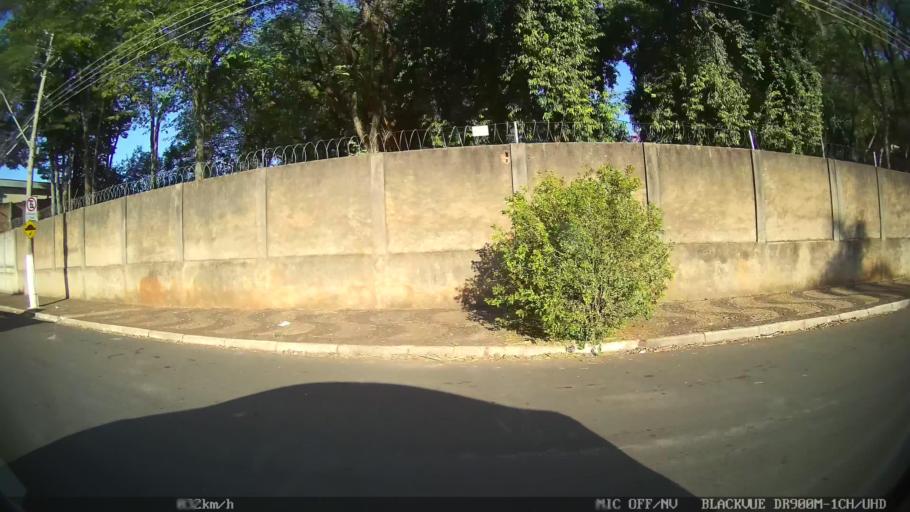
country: BR
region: Sao Paulo
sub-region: Santa Barbara D'Oeste
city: Santa Barbara d'Oeste
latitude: -22.7511
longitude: -47.4247
